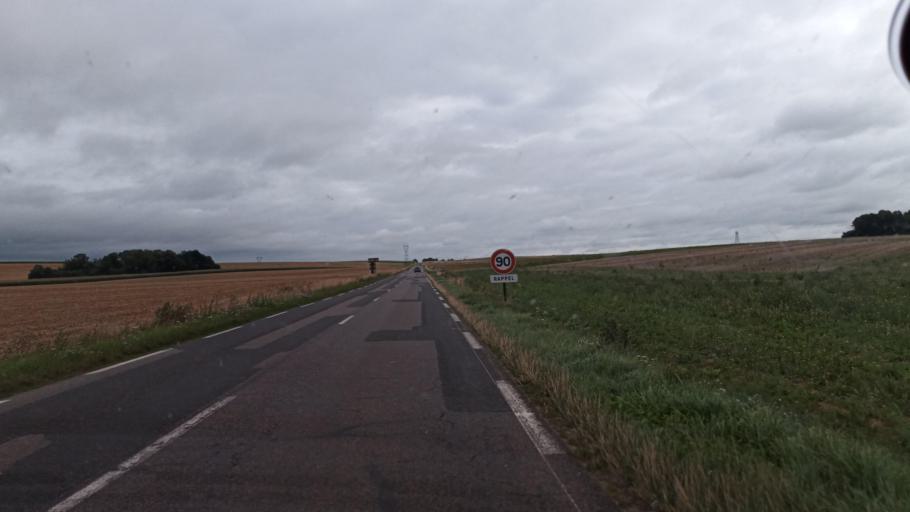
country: FR
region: Ile-de-France
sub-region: Departement de Seine-et-Marne
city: Voulx
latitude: 48.3212
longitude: 2.9519
